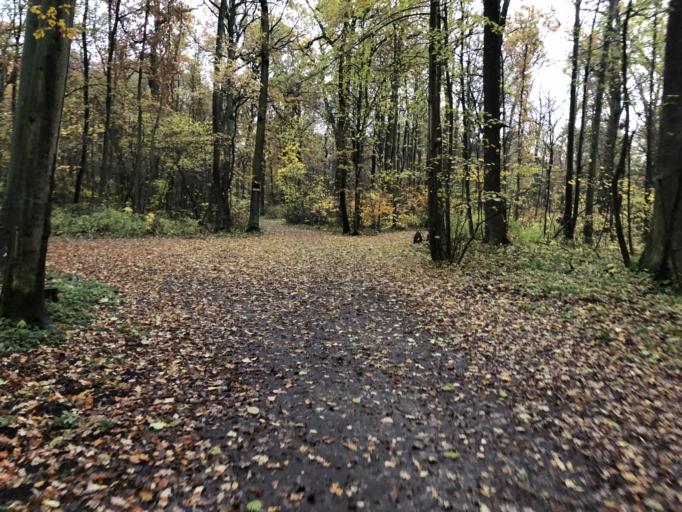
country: DE
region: Saxony-Anhalt
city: Lieskau
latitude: 51.5037
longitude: 11.8927
